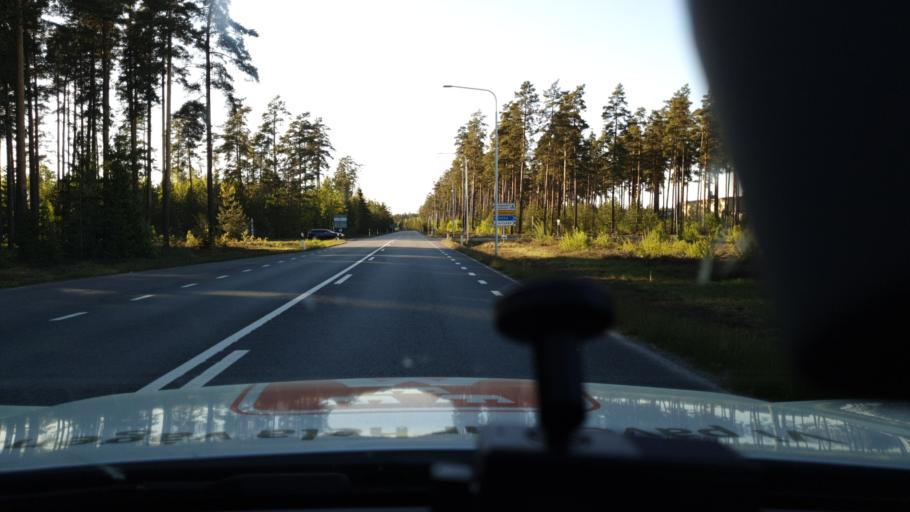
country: SE
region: Joenkoeping
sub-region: Eksjo Kommun
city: Eksjoe
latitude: 57.6359
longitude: 14.9670
